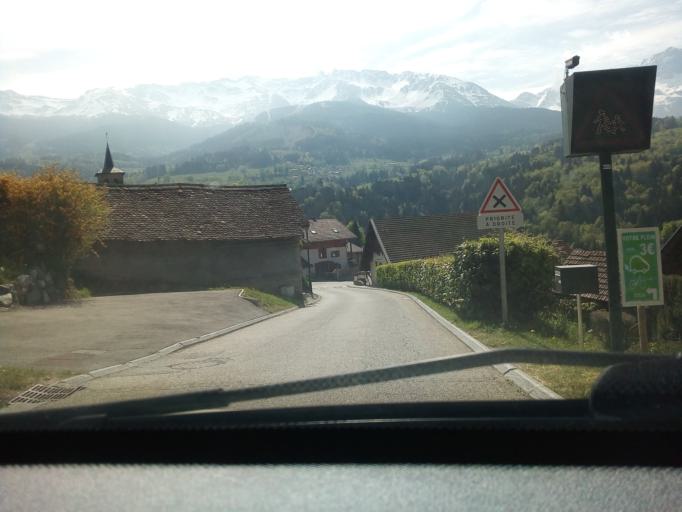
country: FR
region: Rhone-Alpes
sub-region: Departement de l'Isere
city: Le Champ-pres-Froges
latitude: 45.2719
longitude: 5.9634
